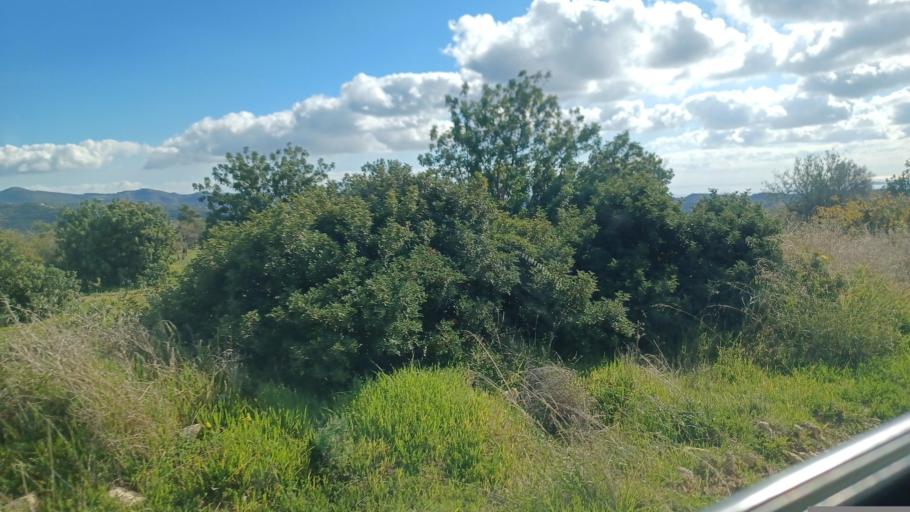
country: CY
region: Limassol
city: Pano Polemidia
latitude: 34.7853
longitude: 32.9818
